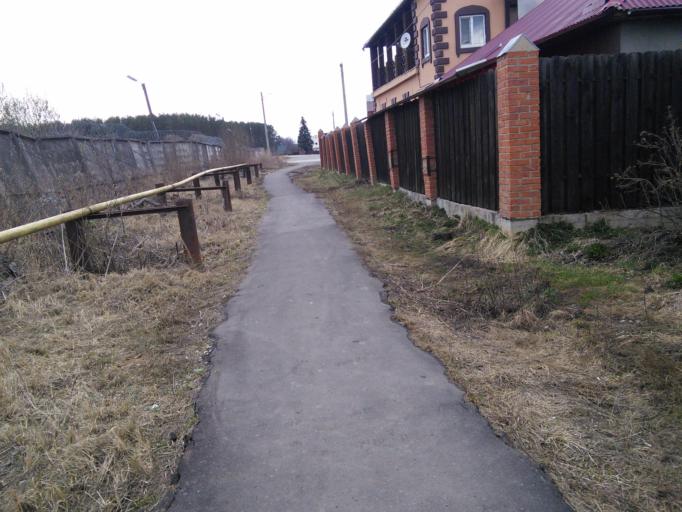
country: RU
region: Moskovskaya
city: Stolbovaya
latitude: 55.2501
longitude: 37.4861
